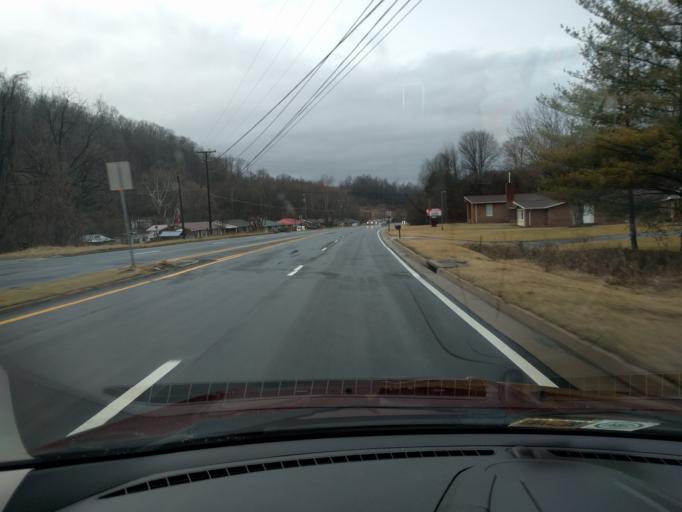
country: US
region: Virginia
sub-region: Giles County
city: Pembroke
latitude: 37.3193
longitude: -80.6178
